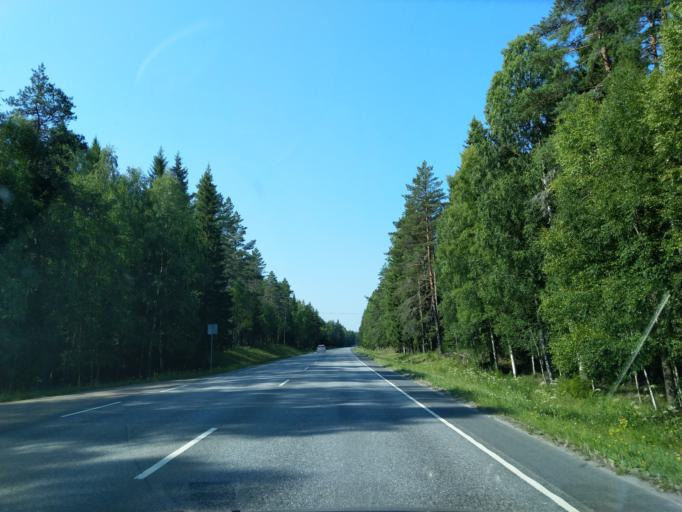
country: FI
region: Satakunta
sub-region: Pori
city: Noormarkku
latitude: 61.6285
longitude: 21.9258
